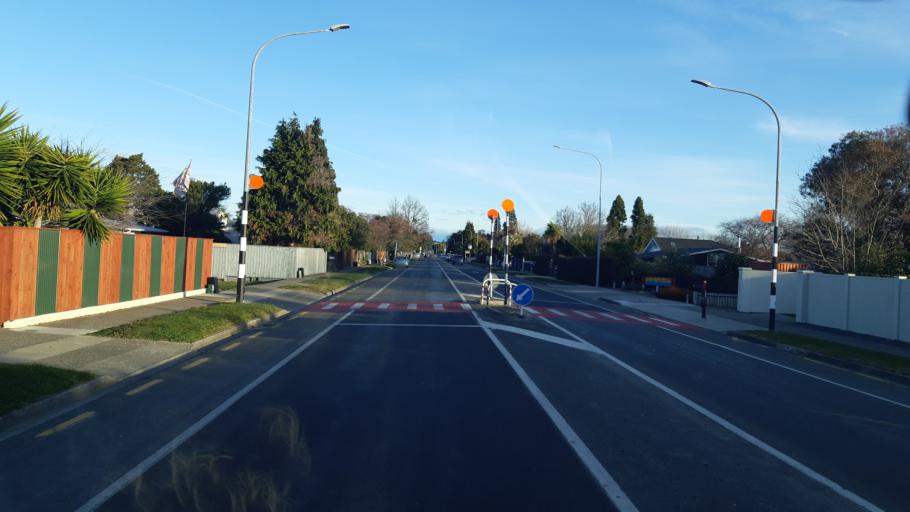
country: NZ
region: Tasman
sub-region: Tasman District
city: Motueka
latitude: -41.1271
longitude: 173.0103
